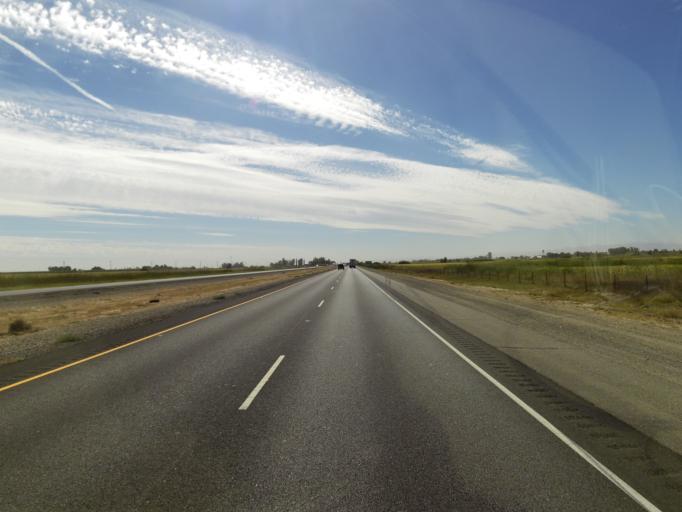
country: US
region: California
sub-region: Colusa County
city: Maxwell
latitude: 39.2976
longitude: -122.1859
